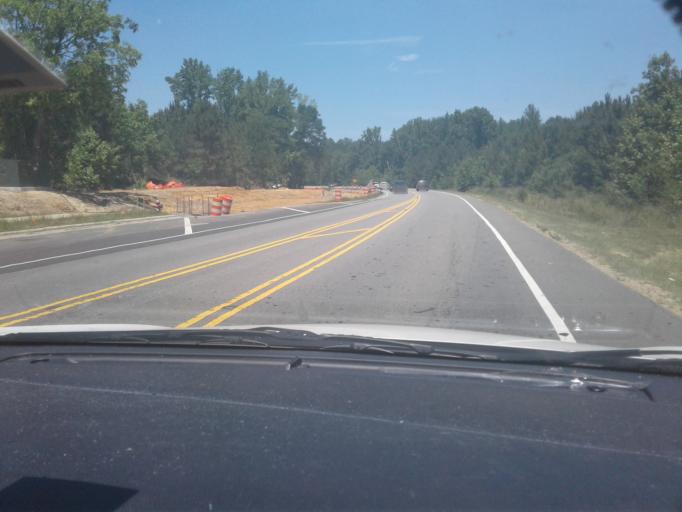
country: US
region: North Carolina
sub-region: Wake County
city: Fuquay-Varina
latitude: 35.5994
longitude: -78.7797
